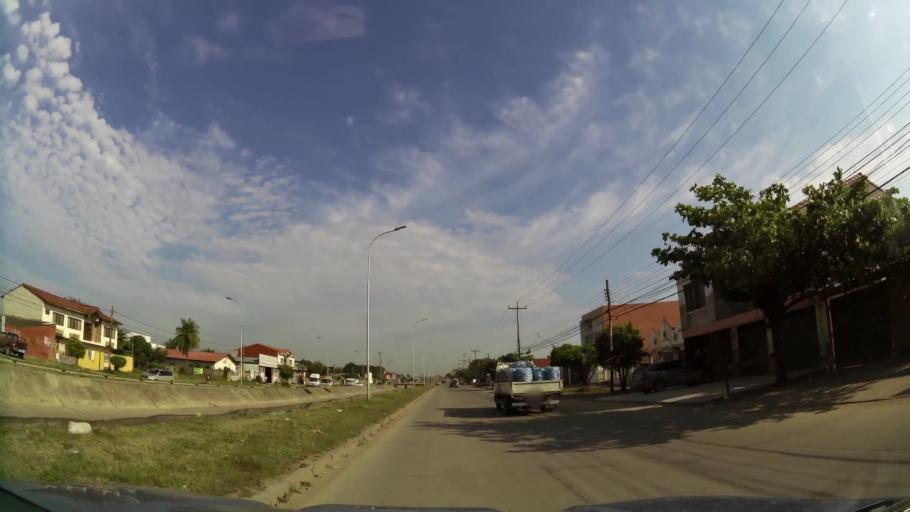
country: BO
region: Santa Cruz
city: Santa Cruz de la Sierra
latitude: -17.7399
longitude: -63.1497
